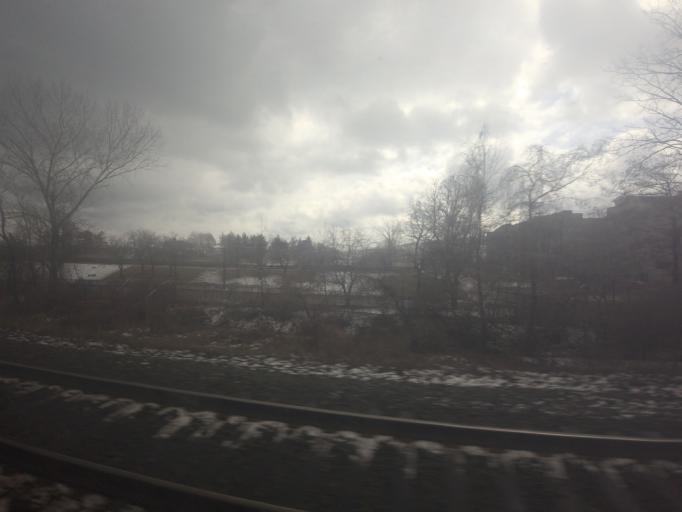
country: CA
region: Ontario
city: Scarborough
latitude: 43.7648
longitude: -79.1511
